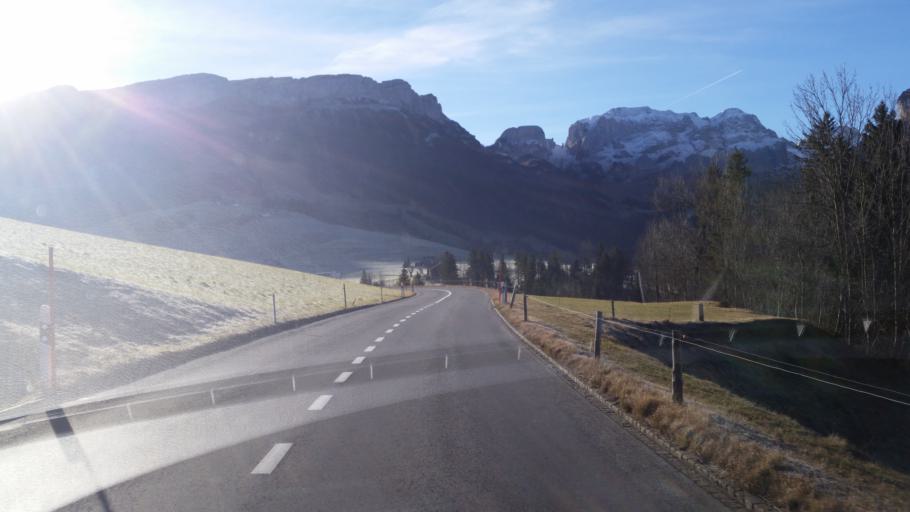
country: CH
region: Appenzell Innerrhoden
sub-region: Appenzell Inner Rhodes
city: Appenzell
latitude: 47.3065
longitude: 9.4443
